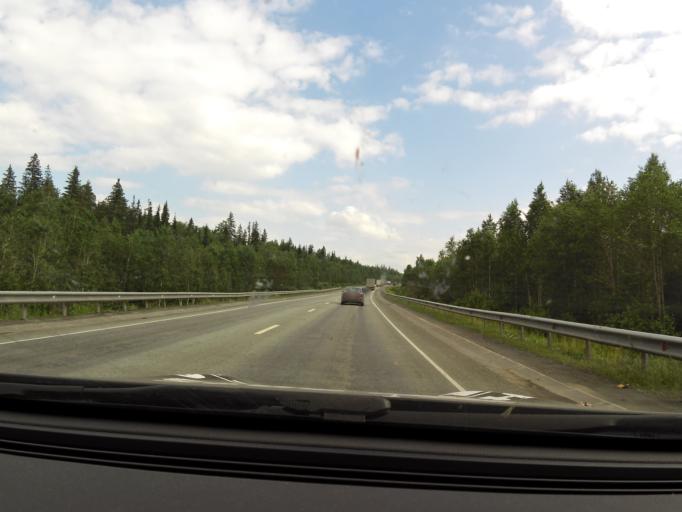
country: RU
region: Sverdlovsk
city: Revda
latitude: 56.8457
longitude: 59.8194
